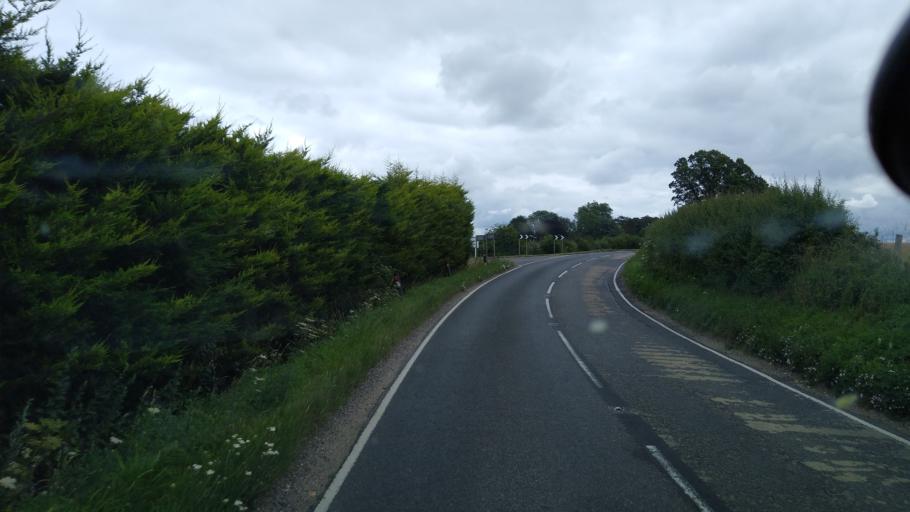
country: GB
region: England
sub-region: Hampshire
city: Alton
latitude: 51.1354
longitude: -0.9748
